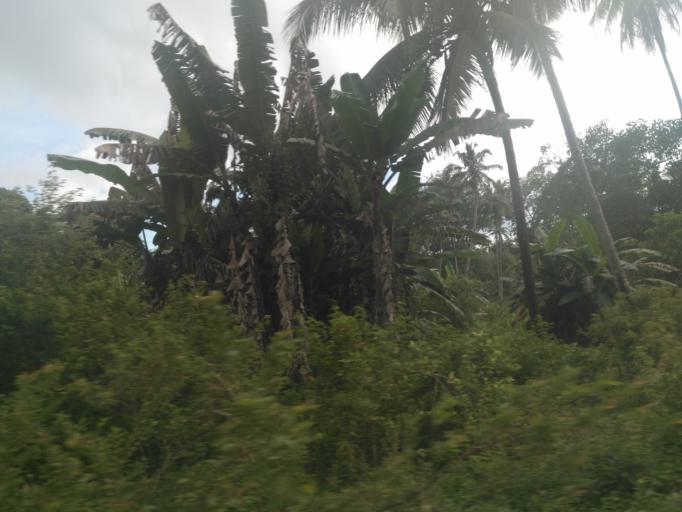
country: TZ
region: Zanzibar Central/South
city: Koani
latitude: -6.1065
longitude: 39.2915
